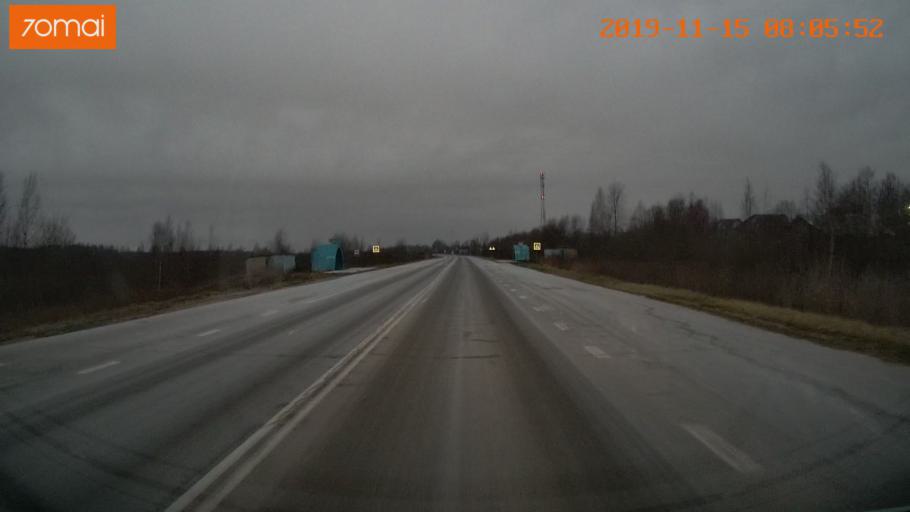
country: RU
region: Vologda
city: Cherepovets
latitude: 59.0190
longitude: 38.0497
